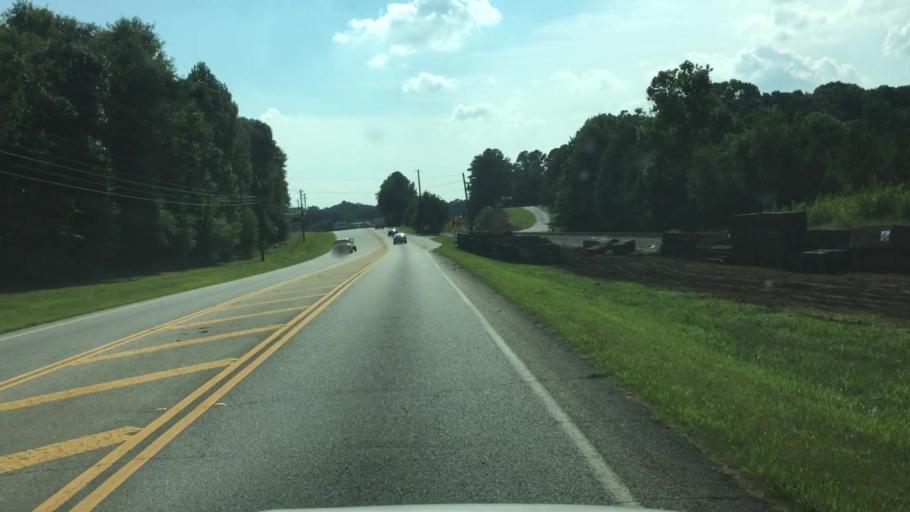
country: US
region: Georgia
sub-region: Barrow County
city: Auburn
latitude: 34.0112
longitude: -83.8450
